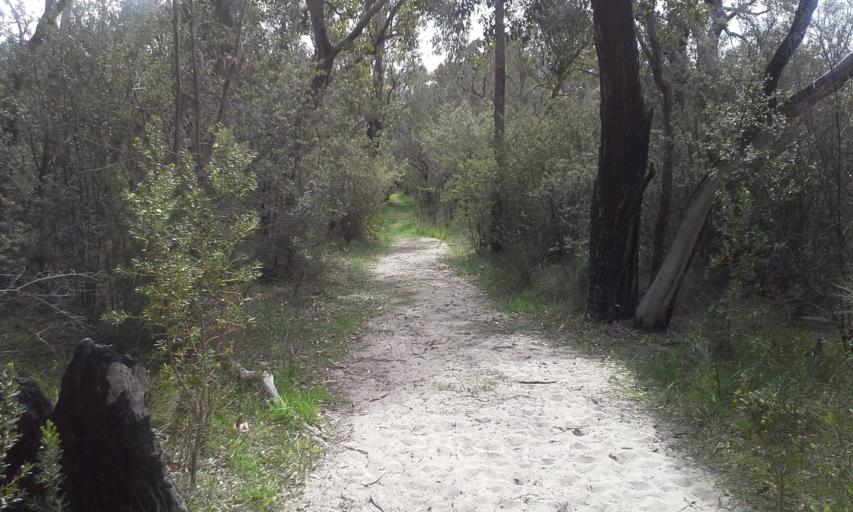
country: AU
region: Western Australia
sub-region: City of Perth
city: West Perth
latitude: -31.9600
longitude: 115.8352
